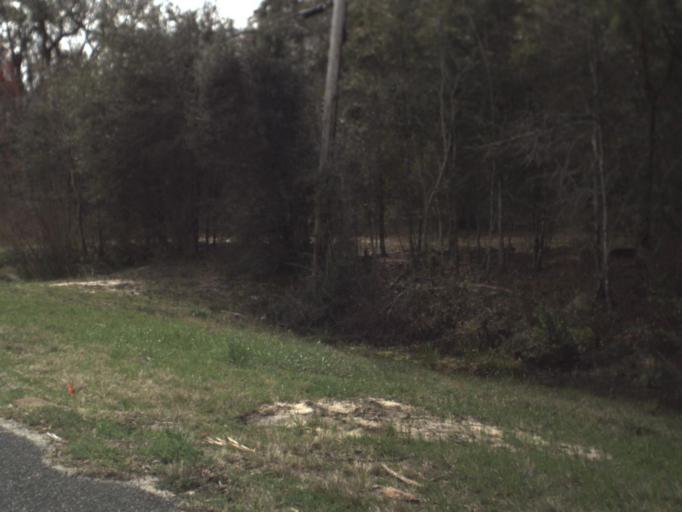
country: US
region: Florida
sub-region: Washington County
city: Chipley
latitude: 30.7252
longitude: -85.3879
